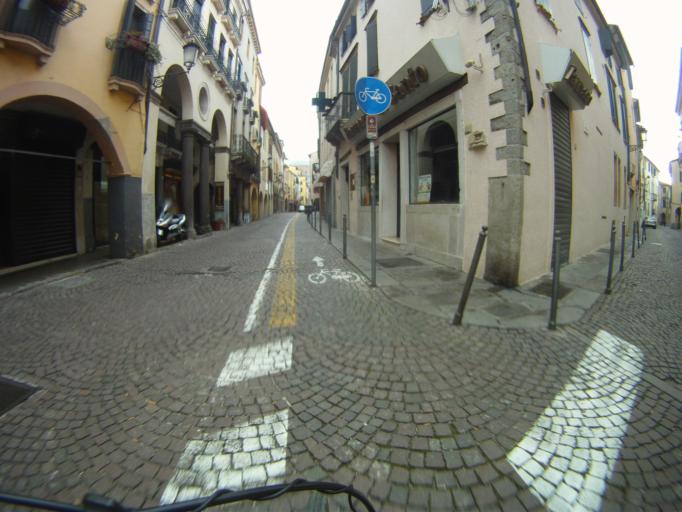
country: IT
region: Veneto
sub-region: Provincia di Padova
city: Padova
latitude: 45.4033
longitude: 11.8791
